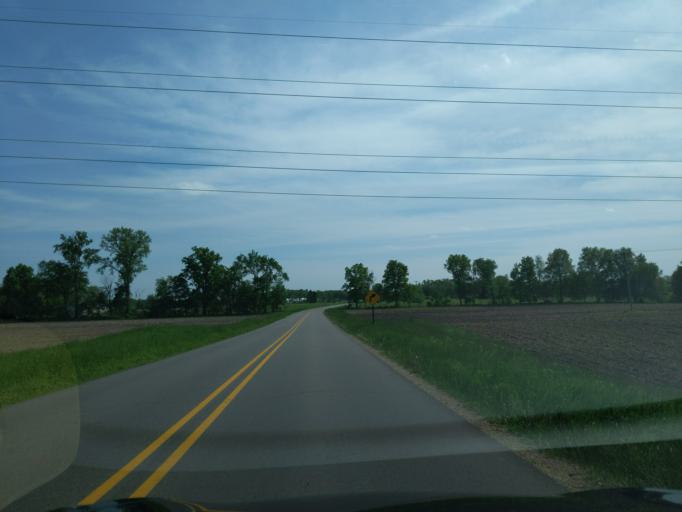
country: US
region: Michigan
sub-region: Ingham County
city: Leslie
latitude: 42.4185
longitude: -84.3124
